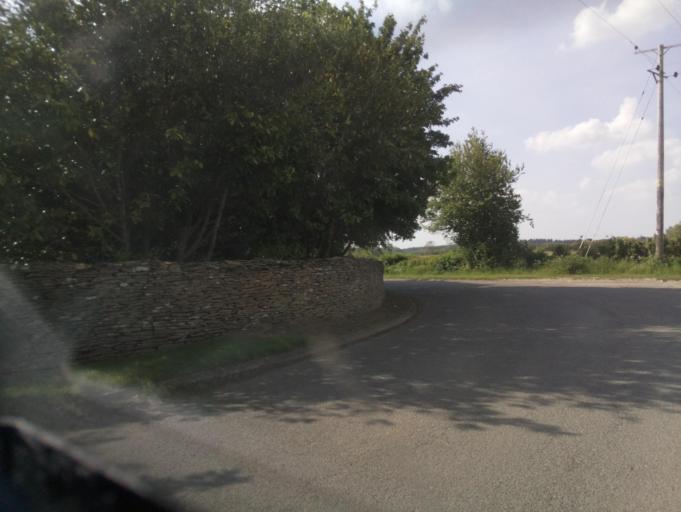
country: GB
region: England
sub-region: Wiltshire
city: Luckington
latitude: 51.5880
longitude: -2.2229
